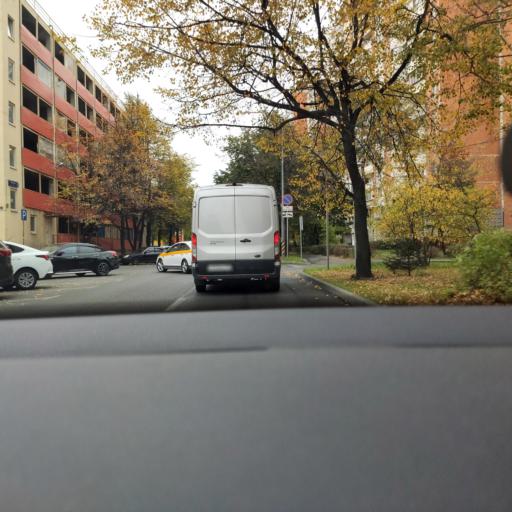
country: RU
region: Moscow
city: Kozeyevo
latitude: 55.8904
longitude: 37.6464
